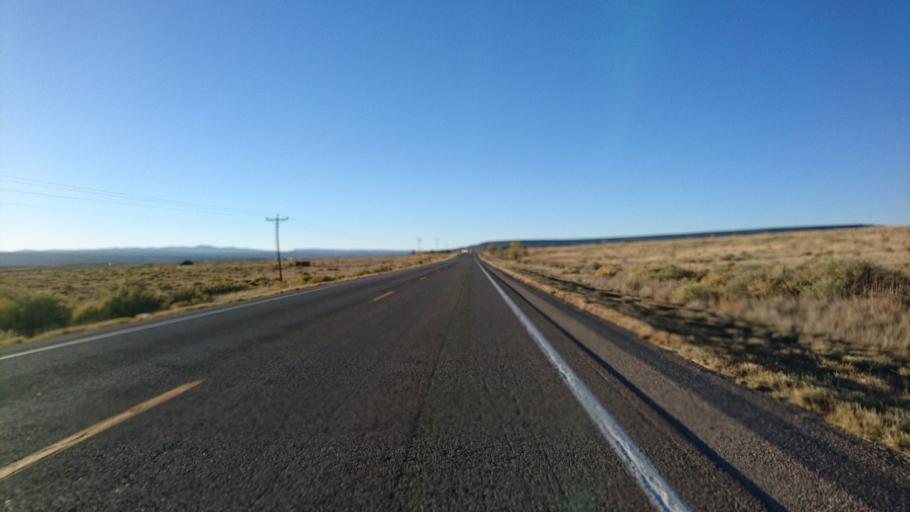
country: US
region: New Mexico
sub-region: Cibola County
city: Grants
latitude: 35.1217
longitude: -107.7965
